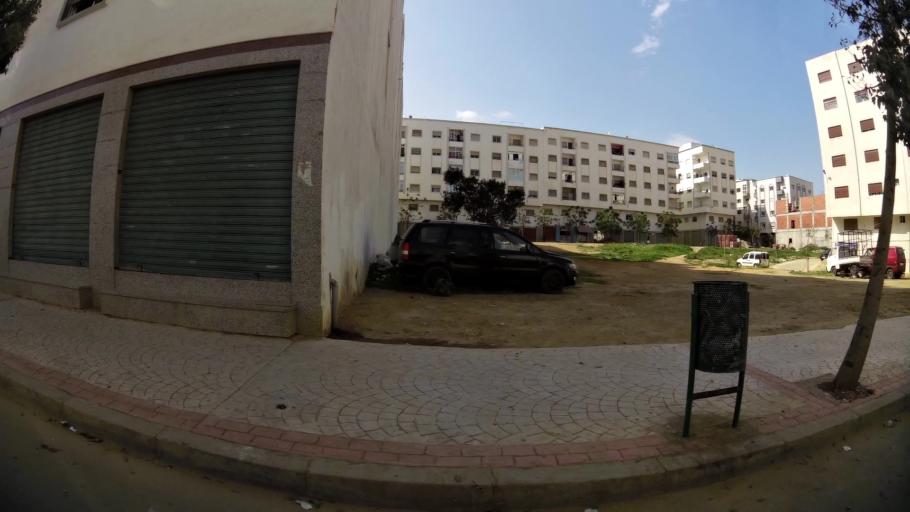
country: MA
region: Tanger-Tetouan
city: Tetouan
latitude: 35.5875
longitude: -5.3562
